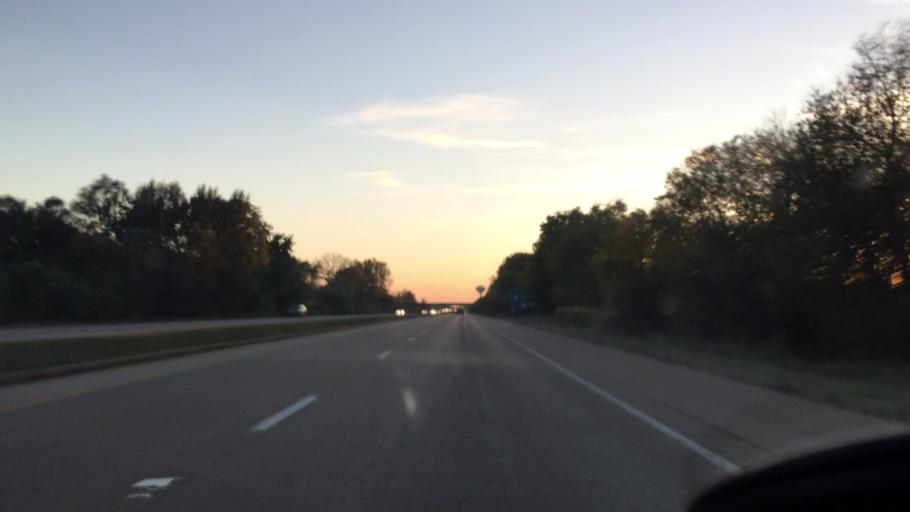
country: US
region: Illinois
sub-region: Grundy County
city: Morris
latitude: 41.4030
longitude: -88.3972
